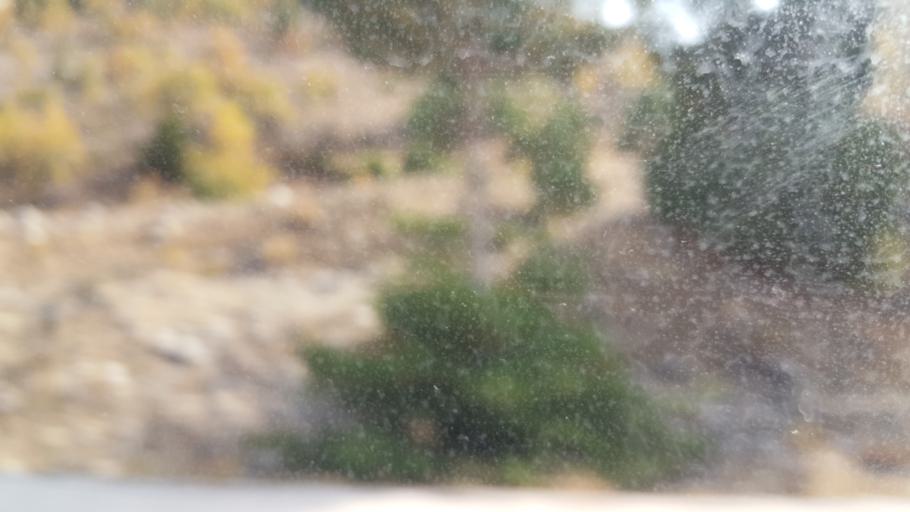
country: TR
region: Eskisehir
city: Mihaliccik
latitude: 39.9761
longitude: 31.3808
